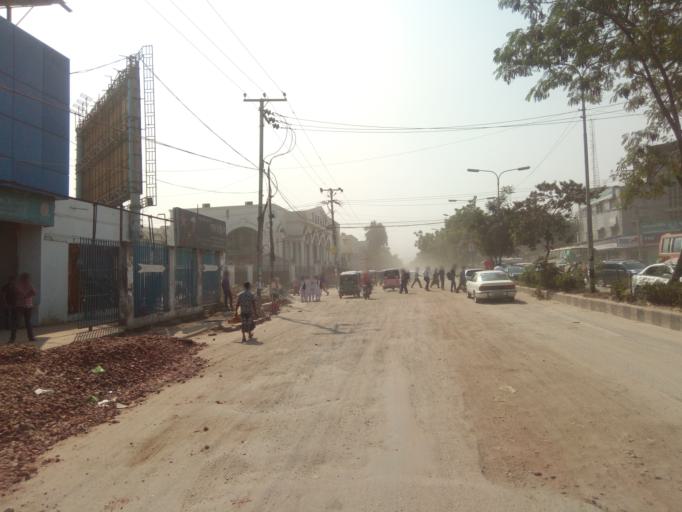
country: BD
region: Dhaka
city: Paltan
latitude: 23.7703
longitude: 90.4013
